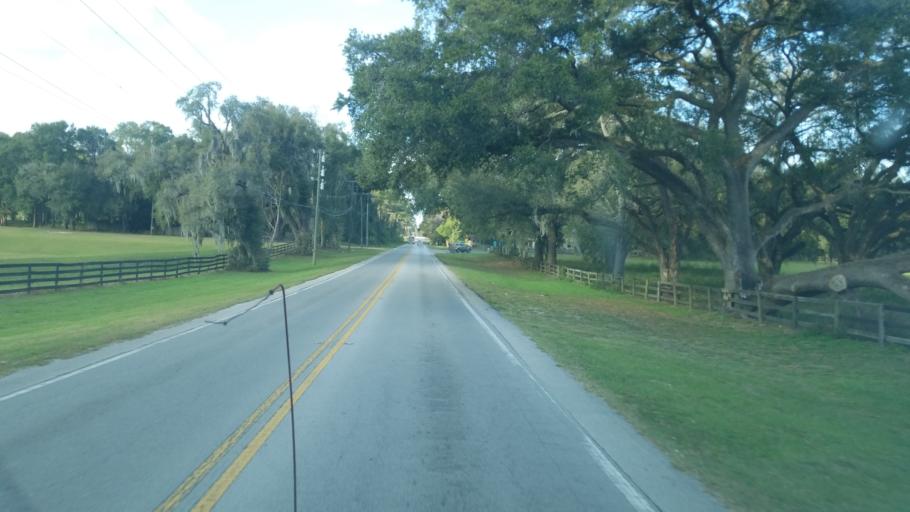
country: US
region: Florida
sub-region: Marion County
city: Ocala
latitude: 29.2763
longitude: -82.1116
